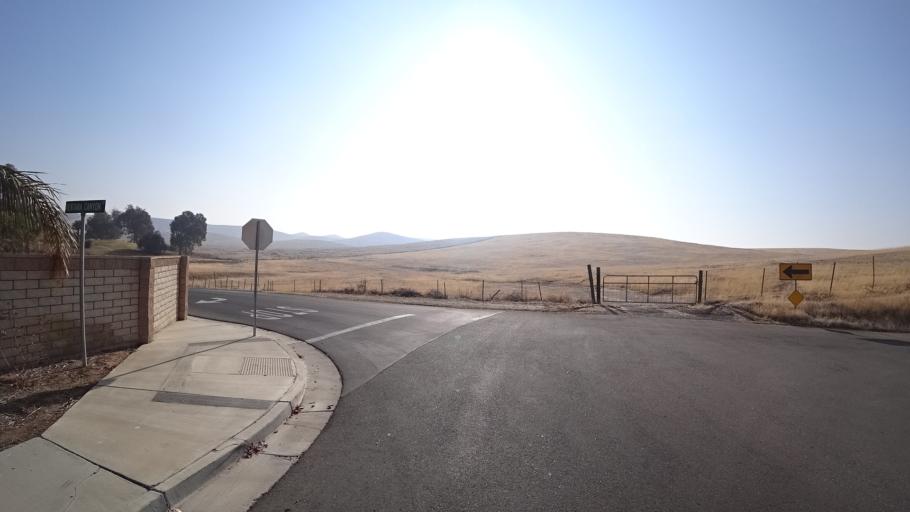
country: US
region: California
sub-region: Kern County
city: Lamont
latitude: 35.3984
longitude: -118.8446
